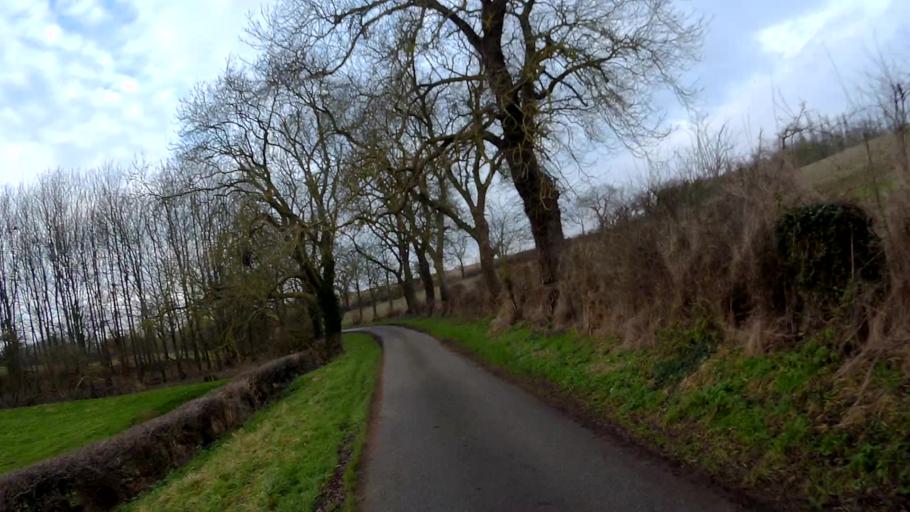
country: GB
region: England
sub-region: Lincolnshire
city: Bourne
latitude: 52.8293
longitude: -0.4705
